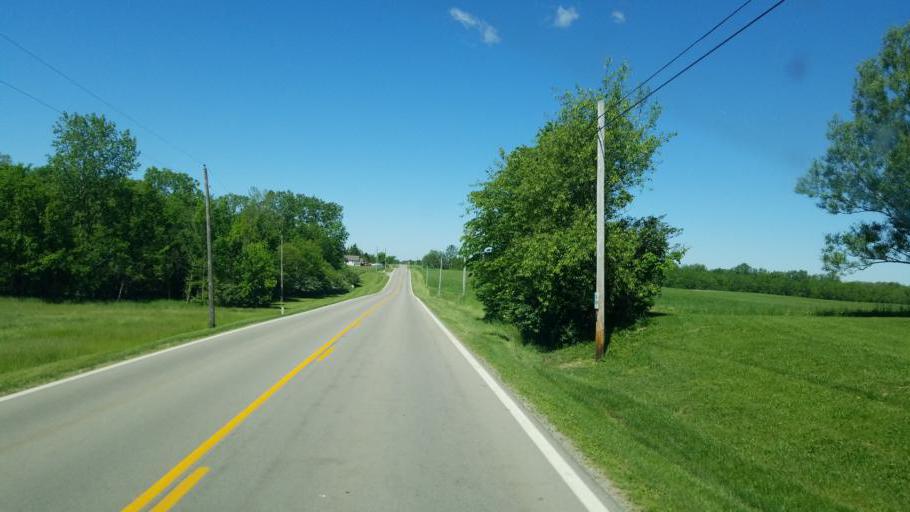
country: US
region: Ohio
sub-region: Logan County
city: Northwood
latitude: 40.4577
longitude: -83.6995
